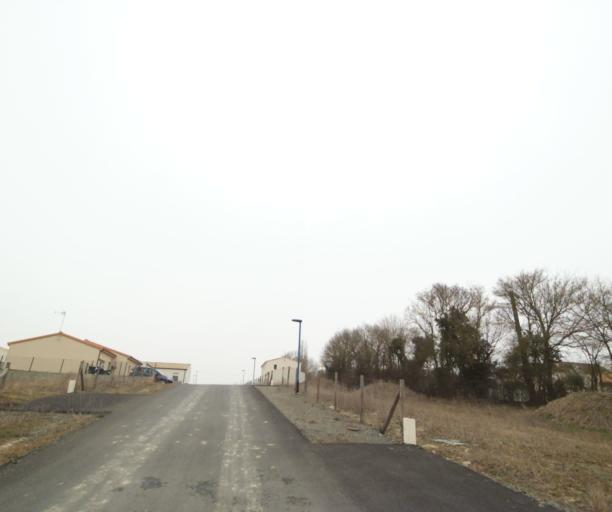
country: FR
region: Poitou-Charentes
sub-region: Departement des Deux-Sevres
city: Bessines
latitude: 46.2978
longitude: -0.4952
